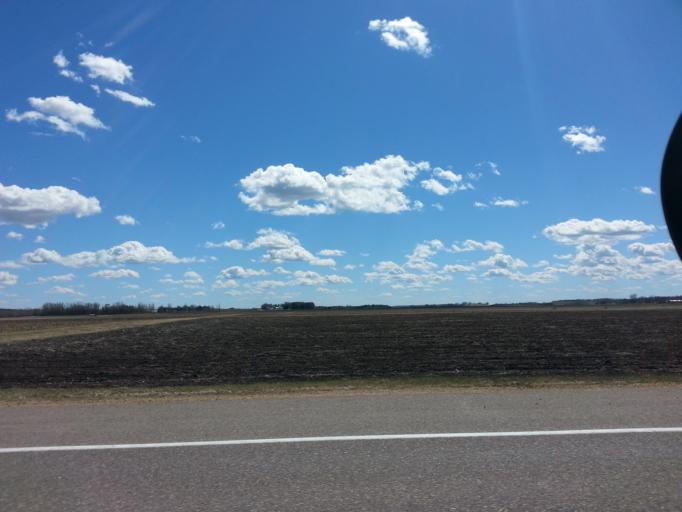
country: US
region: Minnesota
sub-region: Dakota County
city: Rosemount
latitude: 44.7174
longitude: -93.1063
